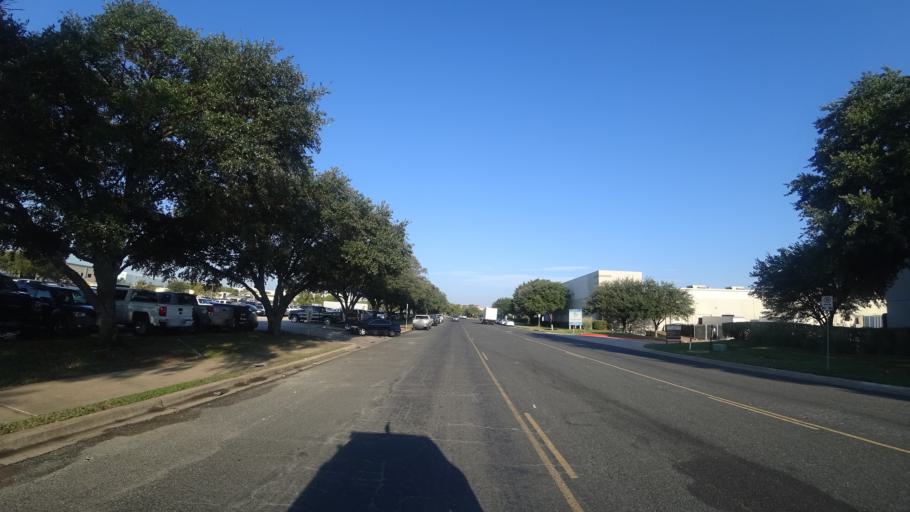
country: US
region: Texas
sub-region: Travis County
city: Manor
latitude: 30.3368
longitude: -97.6591
